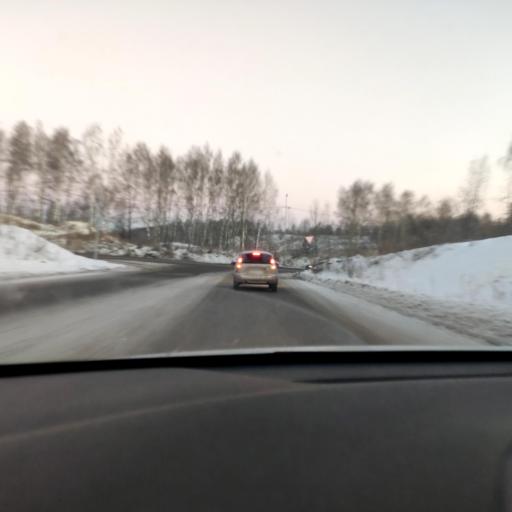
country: RU
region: Tatarstan
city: Osinovo
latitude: 55.8633
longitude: 48.9018
